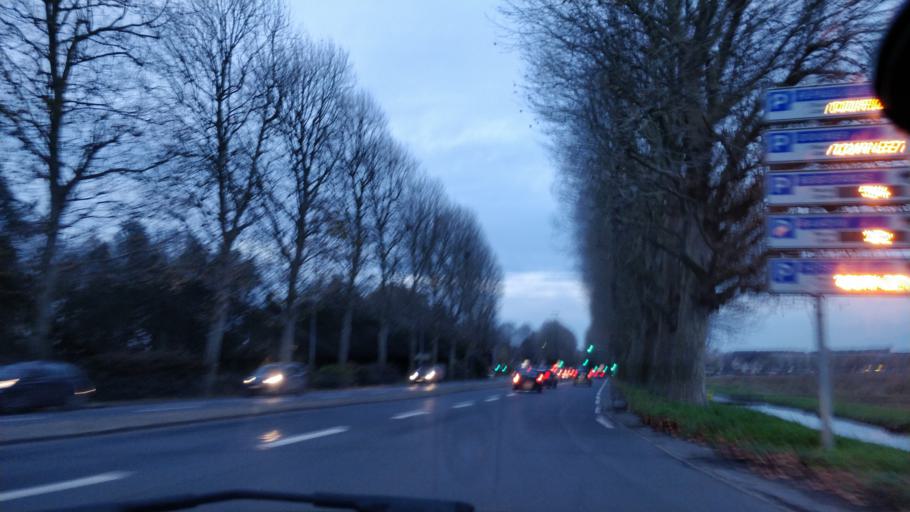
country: FR
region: Lower Normandy
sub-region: Departement du Calvados
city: Caen
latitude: 49.1740
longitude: -0.3726
